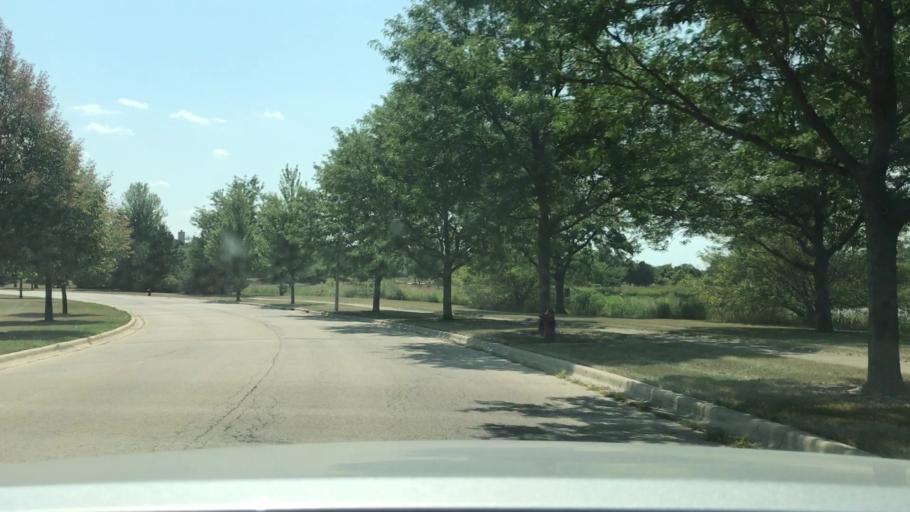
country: US
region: Illinois
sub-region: Kane County
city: Aurora
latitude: 41.7221
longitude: -88.2517
